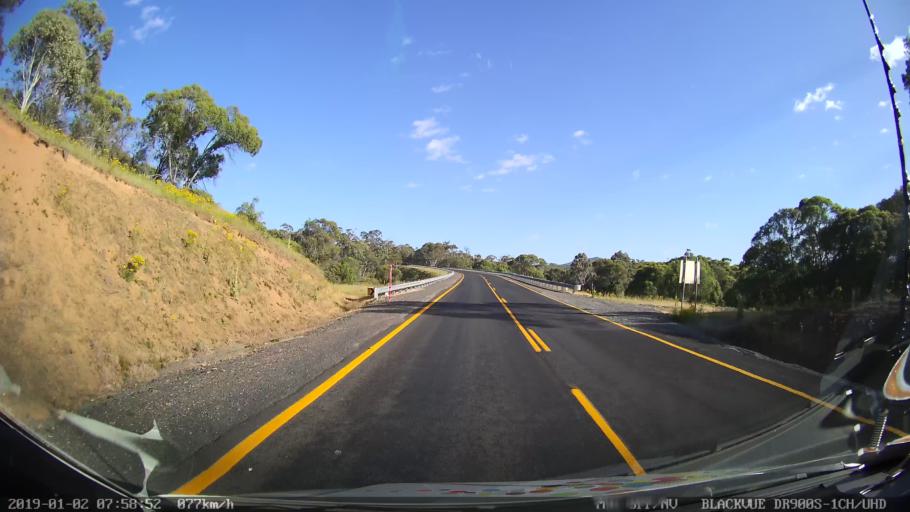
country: AU
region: New South Wales
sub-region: Tumut Shire
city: Tumut
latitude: -35.6496
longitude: 148.4625
